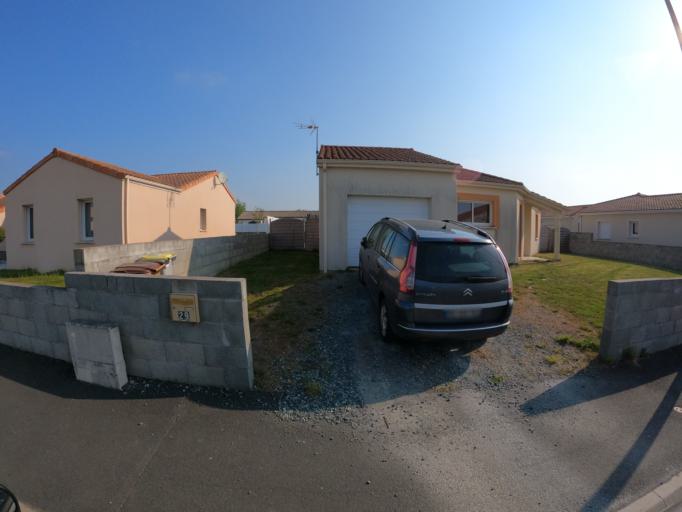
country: FR
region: Pays de la Loire
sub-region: Departement de Maine-et-Loire
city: La Seguiniere
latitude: 47.0669
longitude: -0.9508
